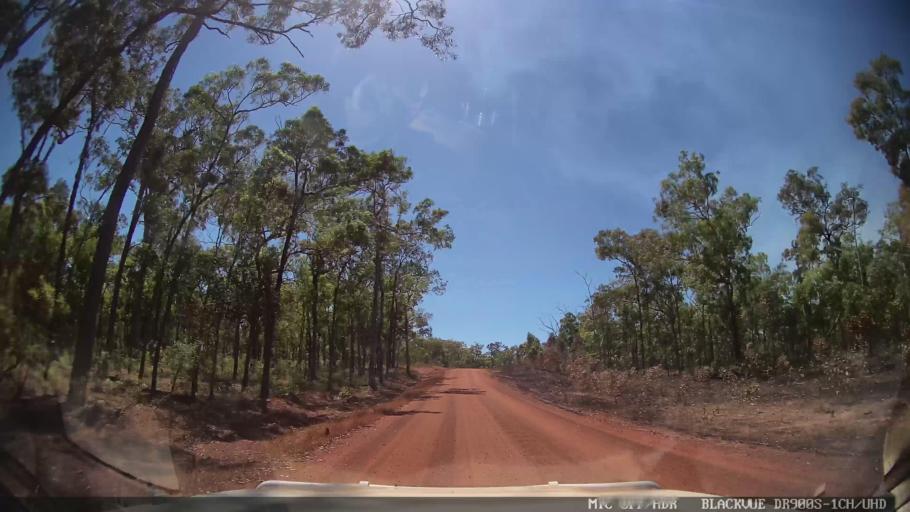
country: AU
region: Queensland
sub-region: Torres
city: Thursday Island
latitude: -10.9709
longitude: 142.3422
